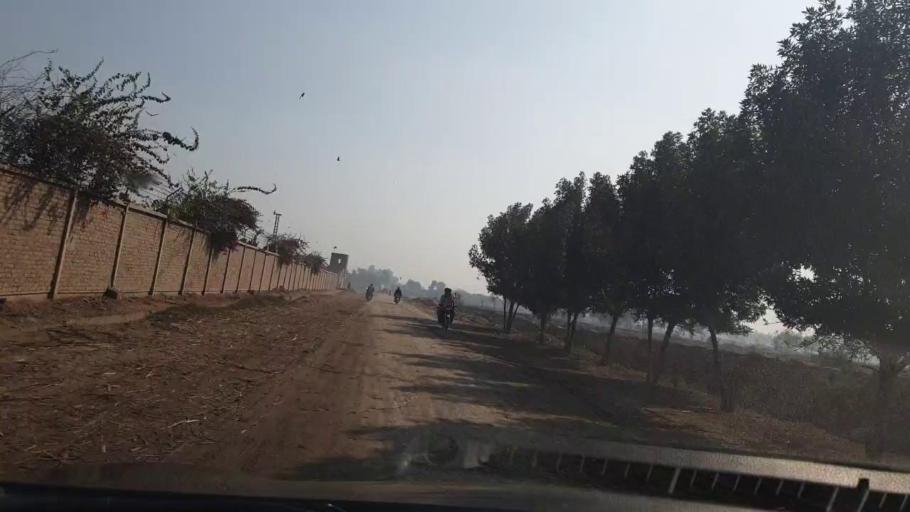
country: PK
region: Sindh
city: Ubauro
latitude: 28.1170
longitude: 69.7206
